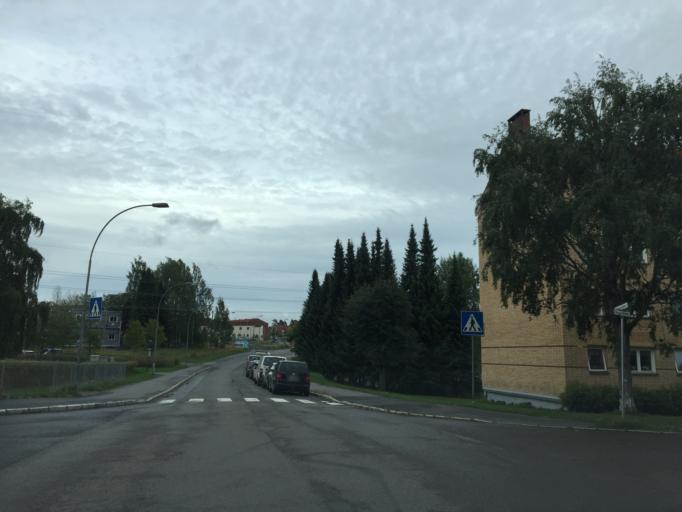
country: NO
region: Oslo
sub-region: Oslo
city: Oslo
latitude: 59.8957
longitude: 10.8179
